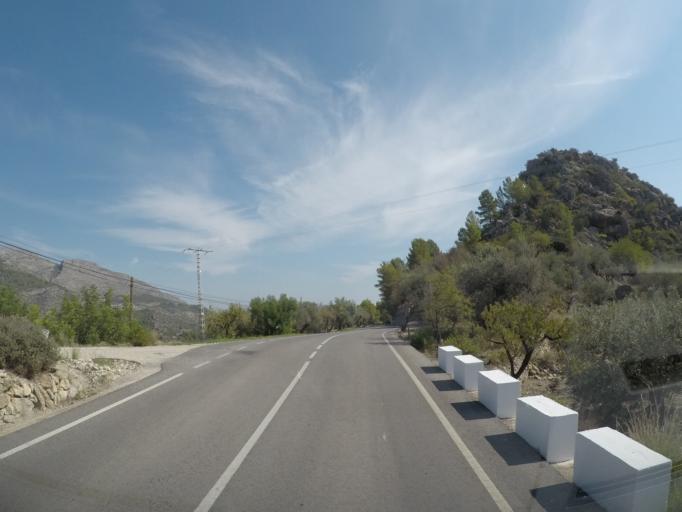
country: ES
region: Valencia
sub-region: Provincia de Alicante
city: Murla
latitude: 38.7813
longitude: -0.0947
